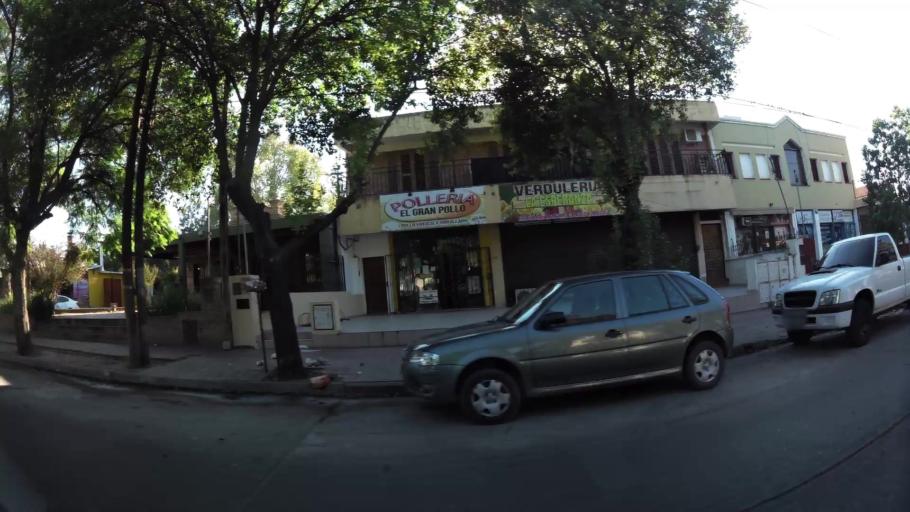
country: AR
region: Cordoba
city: Villa Allende
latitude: -31.3437
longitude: -64.2522
